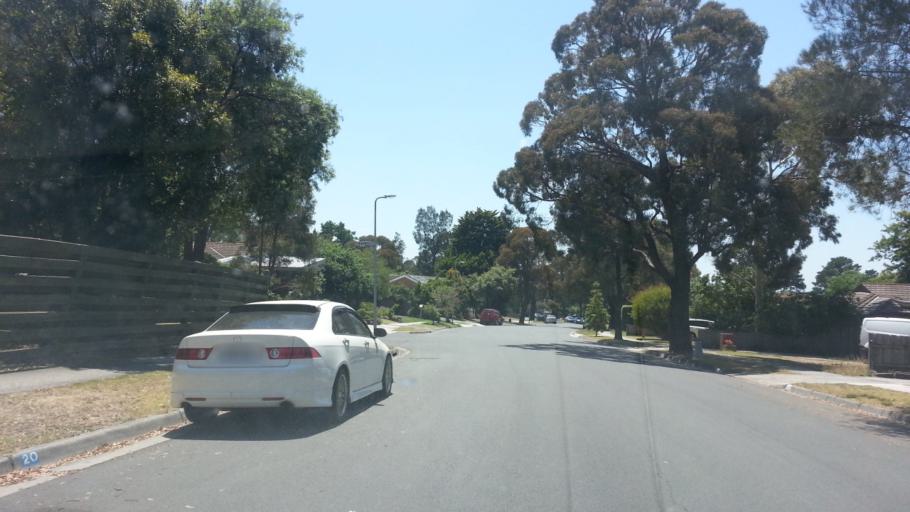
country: AU
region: Victoria
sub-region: Knox
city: Wantirna
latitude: -37.8515
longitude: 145.2328
